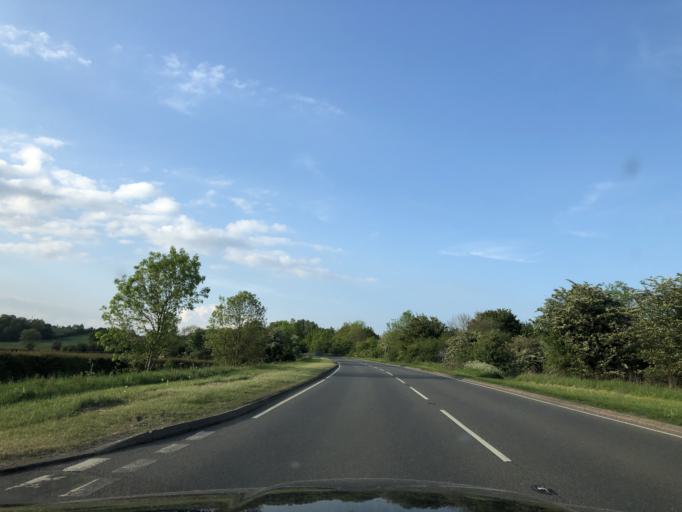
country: GB
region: England
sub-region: Warwickshire
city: Wellesbourne Mountford
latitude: 52.1312
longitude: -1.6147
